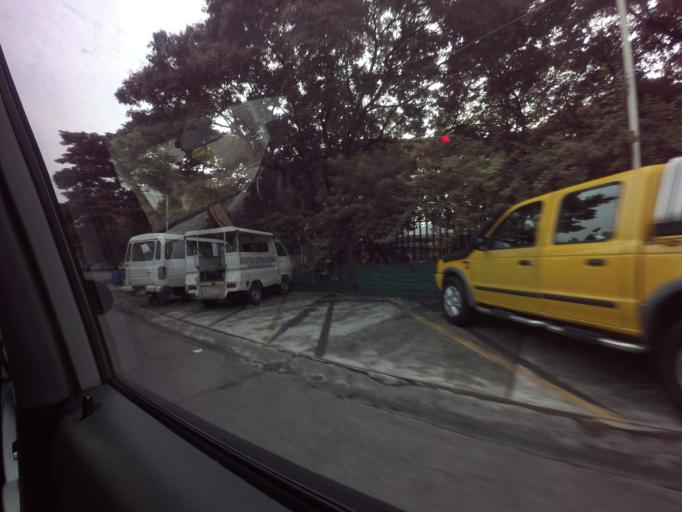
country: PH
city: Sambayanihan People's Village
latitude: 14.4474
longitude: 121.0264
